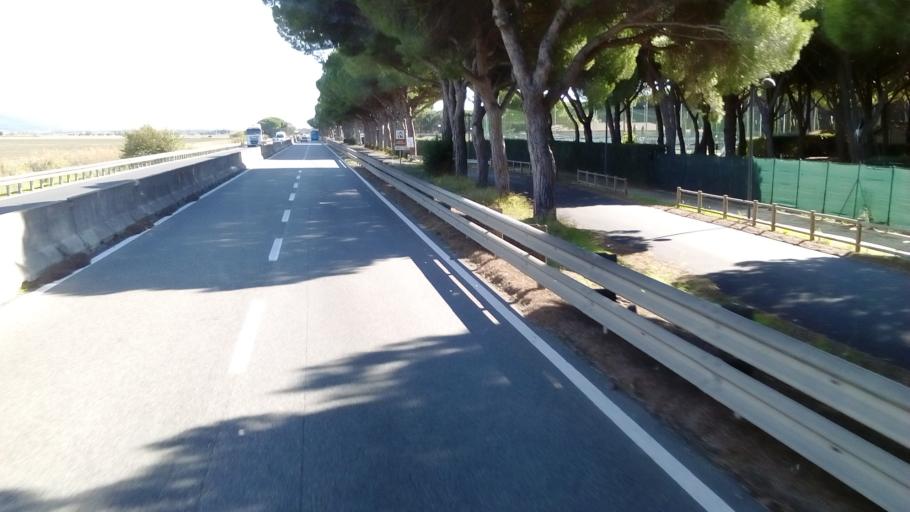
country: IT
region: Tuscany
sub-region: Provincia di Grosseto
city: Albinia
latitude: 42.5308
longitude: 11.1870
